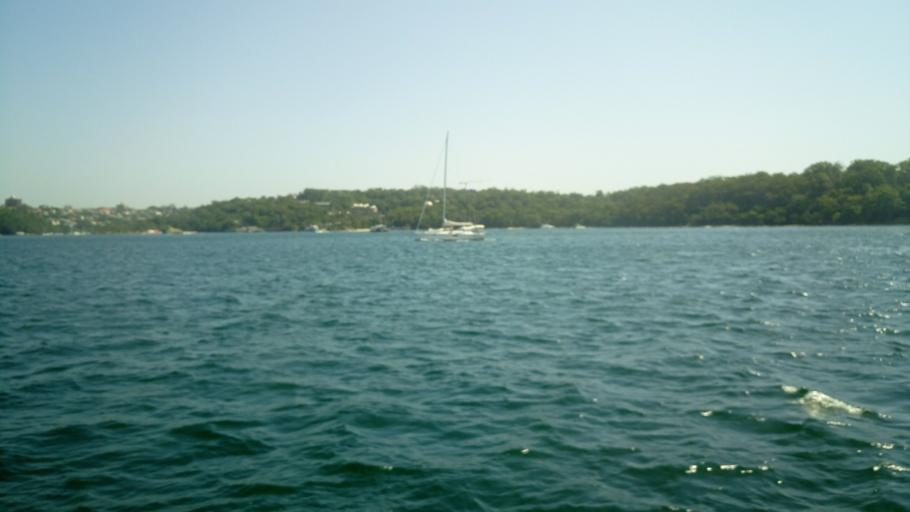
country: AU
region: New South Wales
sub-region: Woollahra
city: Point Piper
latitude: -33.8561
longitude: 151.2405
